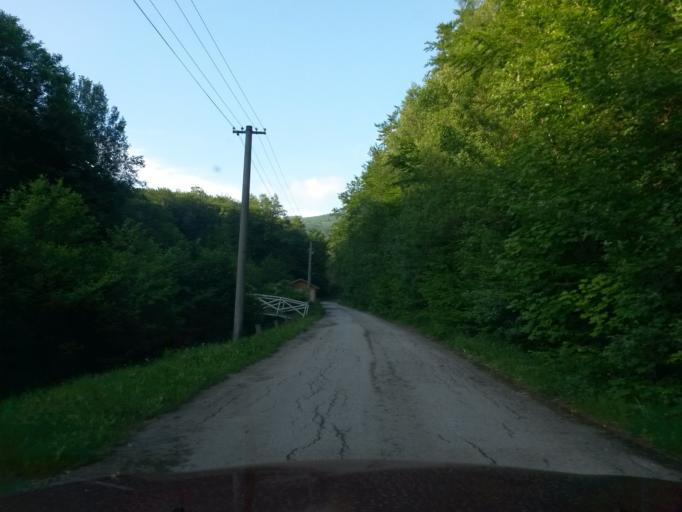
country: SK
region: Kosicky
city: Moldava nad Bodvou
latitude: 48.7432
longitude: 21.0219
